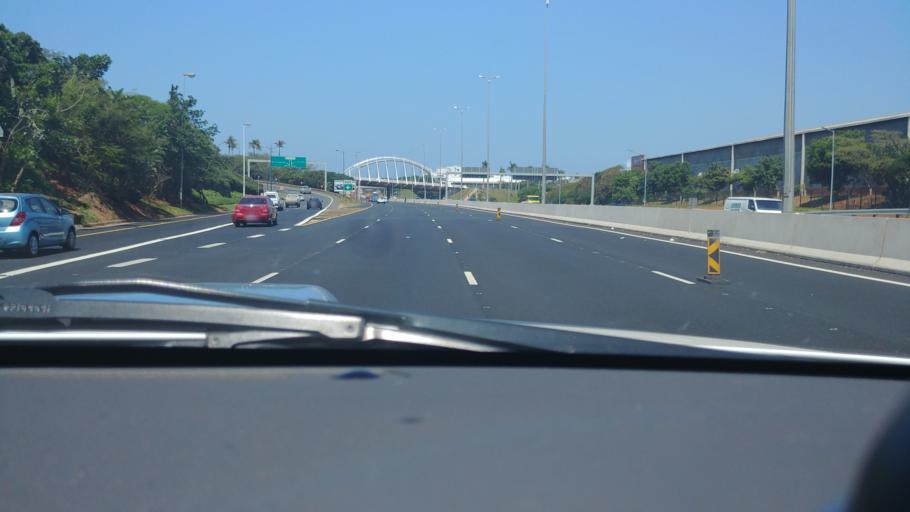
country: ZA
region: KwaZulu-Natal
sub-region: eThekwini Metropolitan Municipality
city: Durban
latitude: -29.7253
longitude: 31.0604
